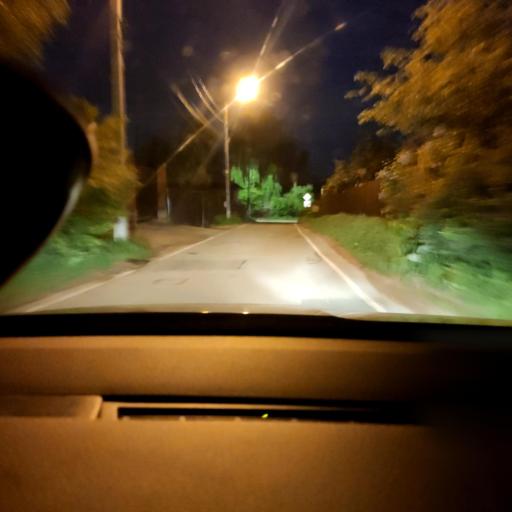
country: RU
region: Moscow
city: Zagor'ye
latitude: 55.5279
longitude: 37.6467
